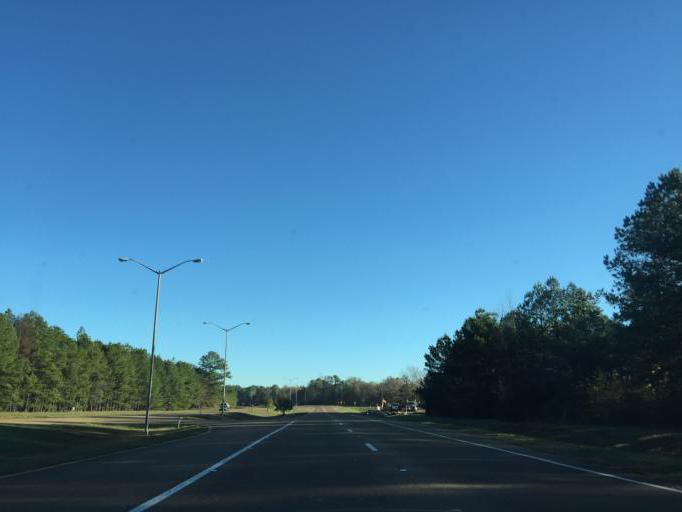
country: US
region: Mississippi
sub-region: Rankin County
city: Flowood
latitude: 32.2918
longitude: -90.1482
